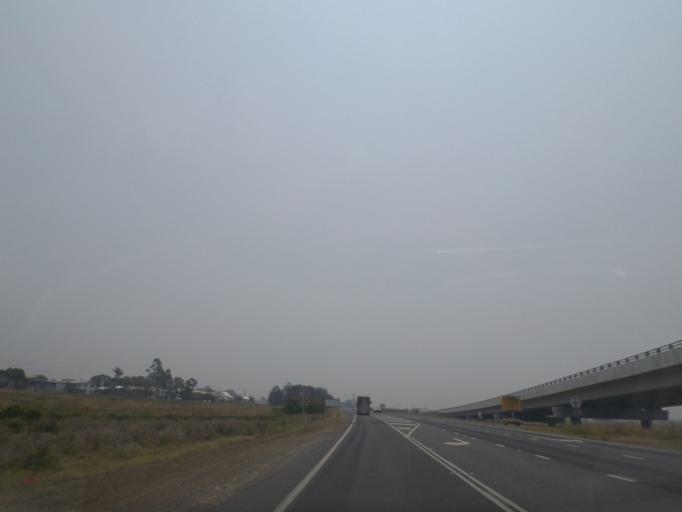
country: AU
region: New South Wales
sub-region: Clarence Valley
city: Maclean
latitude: -29.4247
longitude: 153.2412
